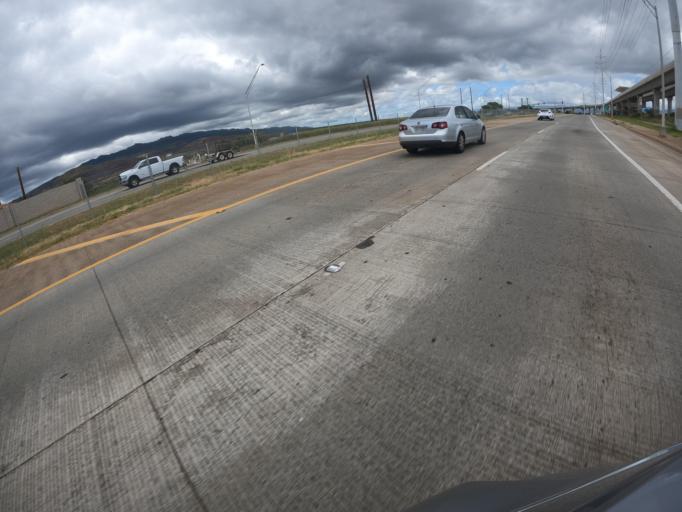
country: US
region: Hawaii
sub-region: Honolulu County
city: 'Ewa Villages
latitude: 21.3439
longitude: -158.0518
